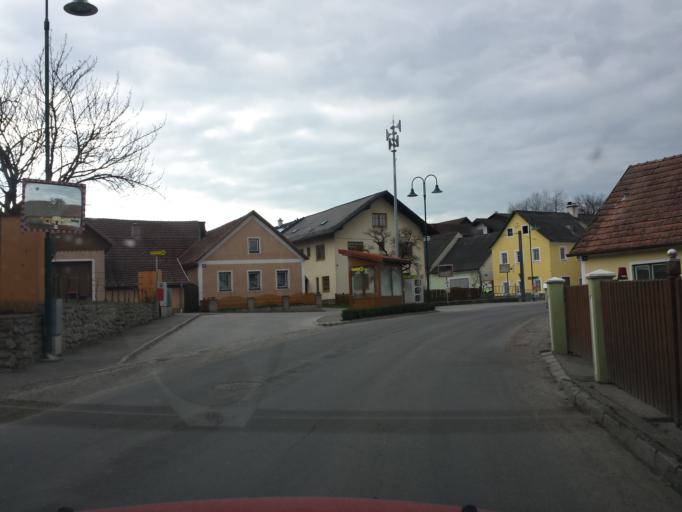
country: AT
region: Lower Austria
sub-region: Politischer Bezirk Krems
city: Rastenfeld
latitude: 48.5445
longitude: 15.3493
